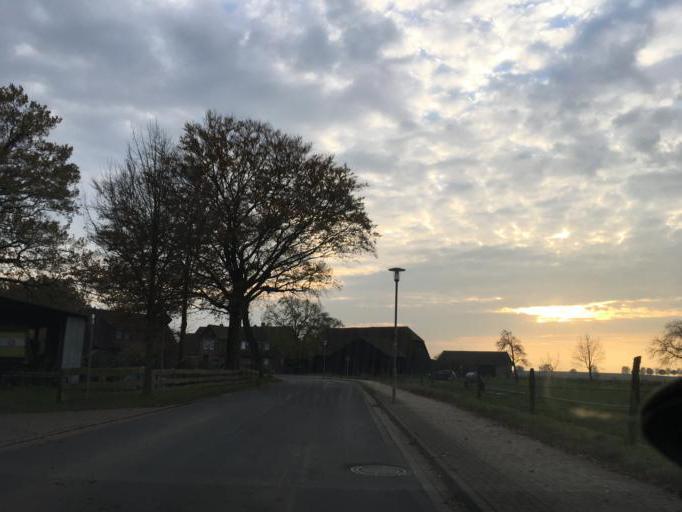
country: DE
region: Lower Saxony
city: Bergen
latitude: 52.8444
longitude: 9.9727
